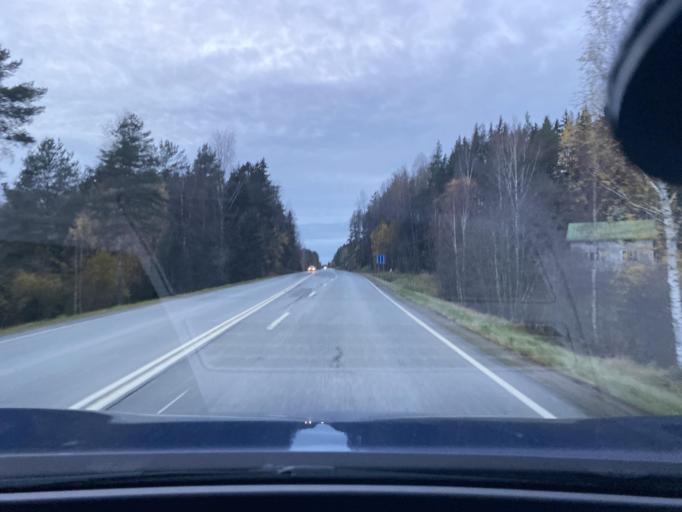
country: FI
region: Uusimaa
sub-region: Helsinki
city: Sammatti
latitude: 60.3851
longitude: 23.8727
